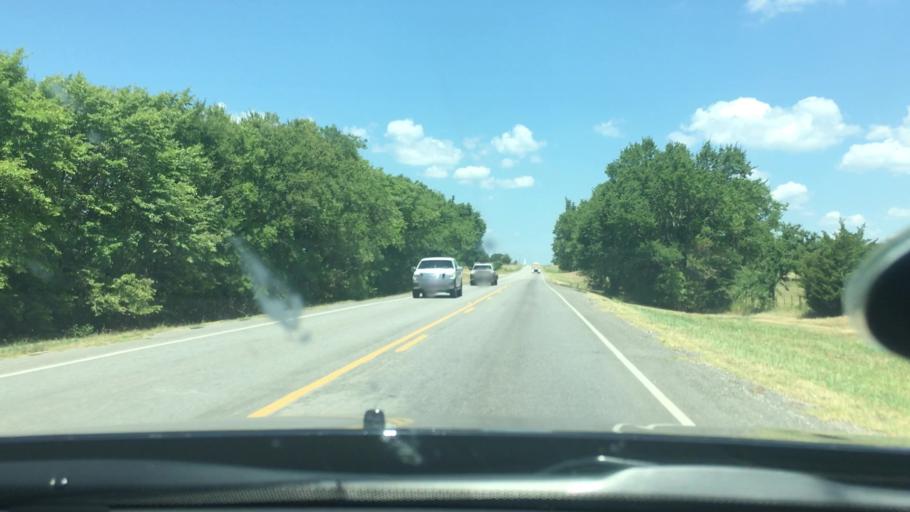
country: US
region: Oklahoma
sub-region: Marshall County
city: Oakland
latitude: 34.1229
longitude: -96.7829
